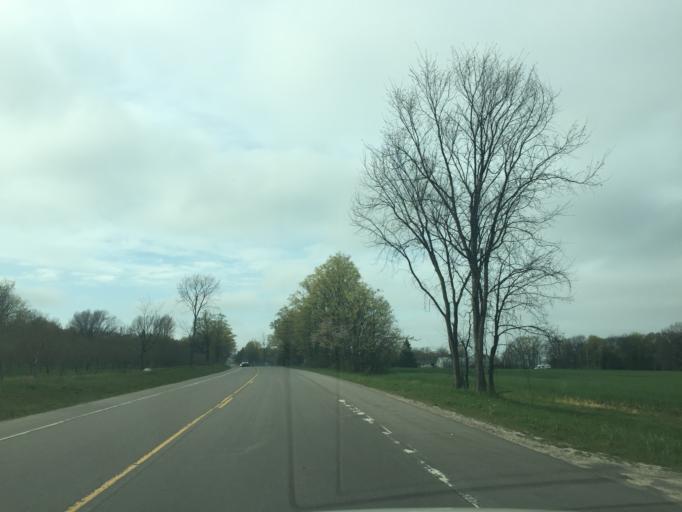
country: US
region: Michigan
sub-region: Leelanau County
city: Leland
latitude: 45.0727
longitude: -85.5885
